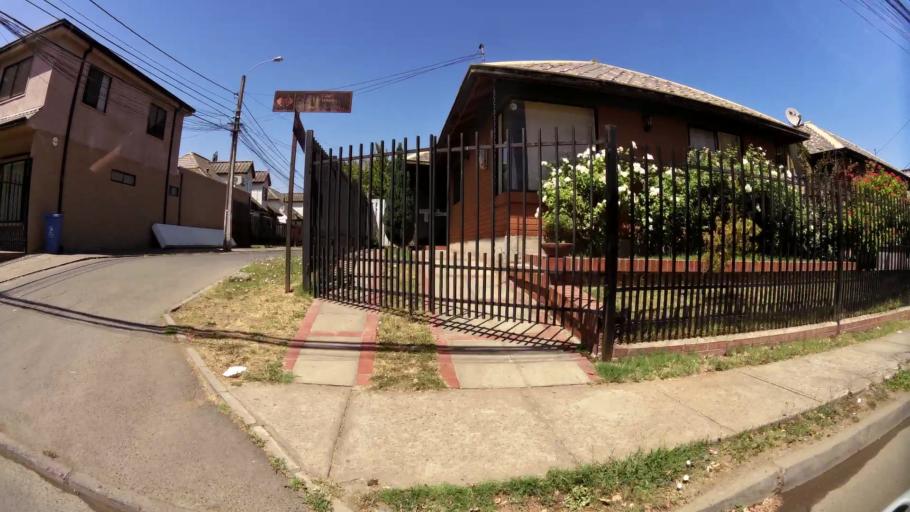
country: CL
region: Maule
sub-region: Provincia de Talca
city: Talca
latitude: -35.4291
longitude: -71.6246
